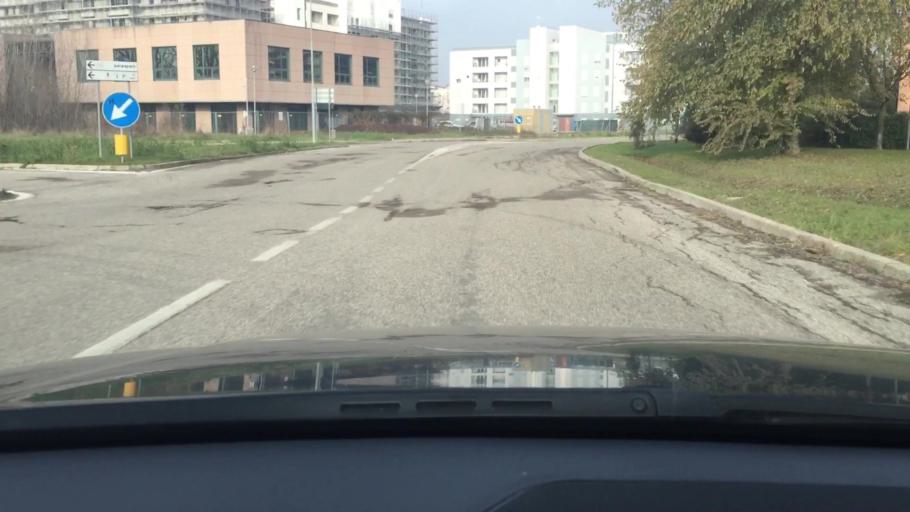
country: IT
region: Emilia-Romagna
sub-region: Provincia di Ferrara
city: Ferrara
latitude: 44.8187
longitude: 11.5966
